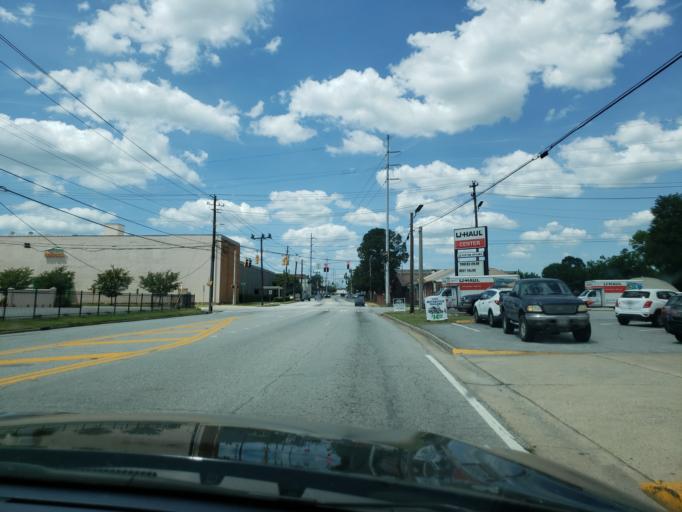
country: US
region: Georgia
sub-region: Muscogee County
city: Columbus
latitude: 32.4640
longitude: -84.9797
